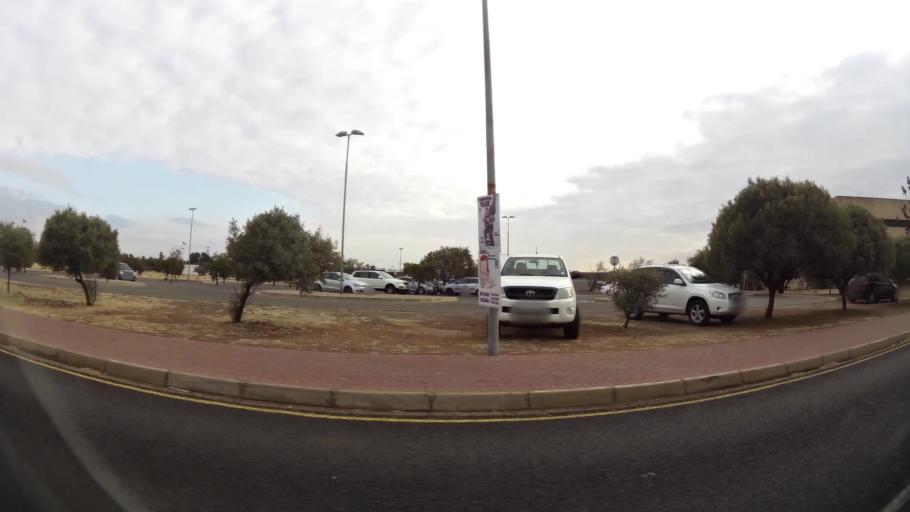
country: ZA
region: Orange Free State
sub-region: Mangaung Metropolitan Municipality
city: Bloemfontein
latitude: -29.1108
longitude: 26.1818
